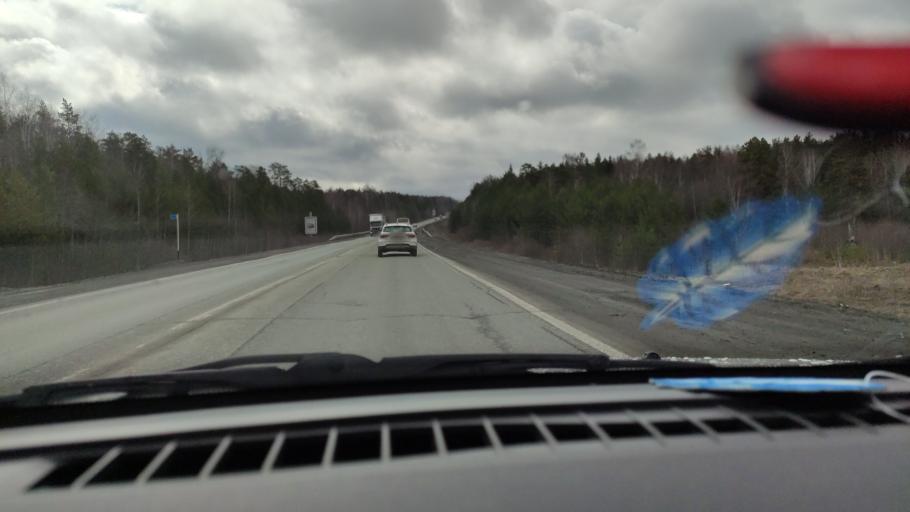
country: RU
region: Sverdlovsk
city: Talitsa
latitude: 56.8637
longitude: 60.0494
